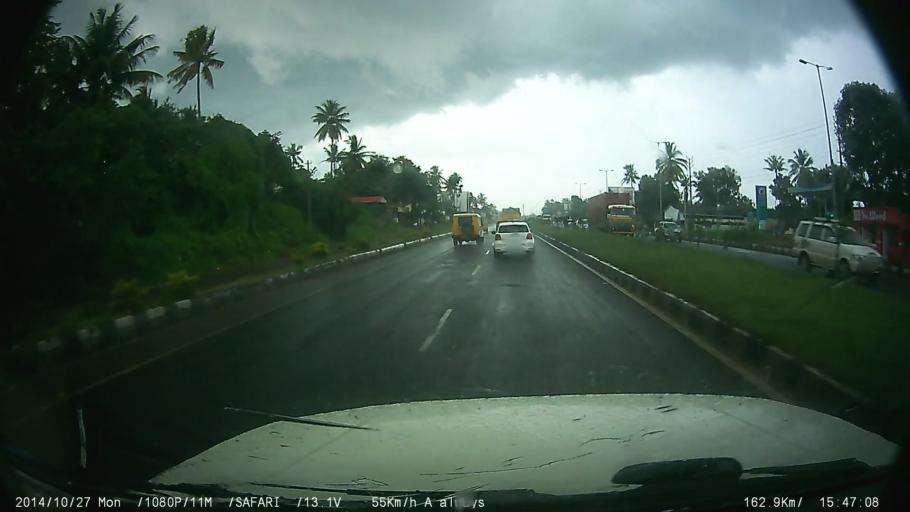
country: IN
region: Kerala
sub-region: Ernakulam
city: Angamali
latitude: 10.2184
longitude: 76.3773
